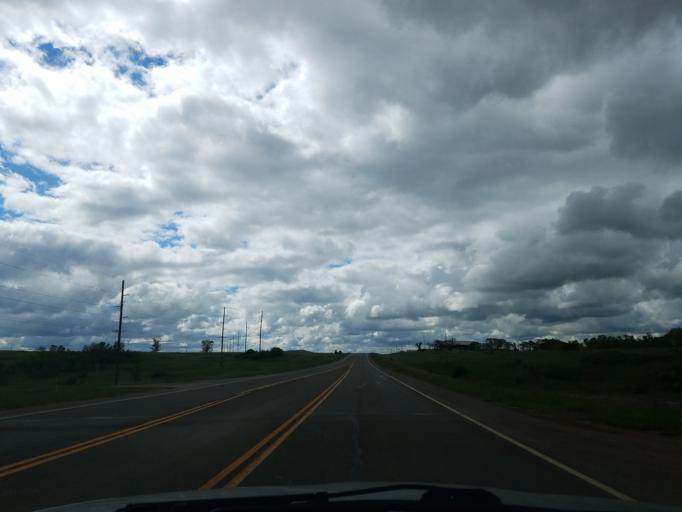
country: US
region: North Dakota
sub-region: McKenzie County
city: Watford City
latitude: 47.3921
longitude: -103.2434
